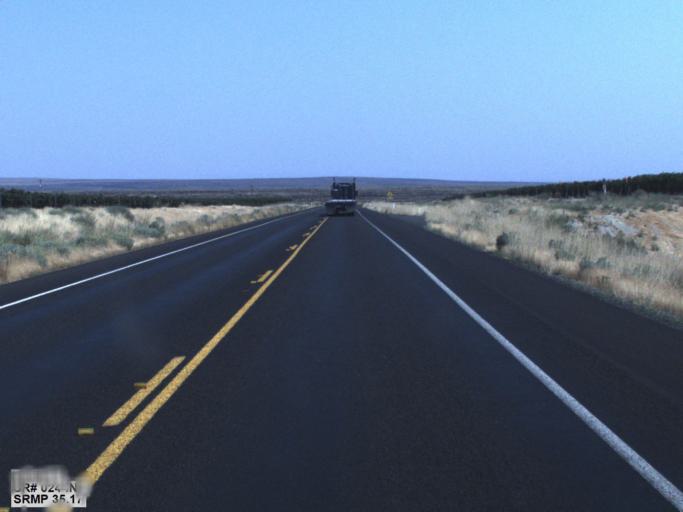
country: US
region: Washington
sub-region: Grant County
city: Desert Aire
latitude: 46.5671
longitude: -119.7958
